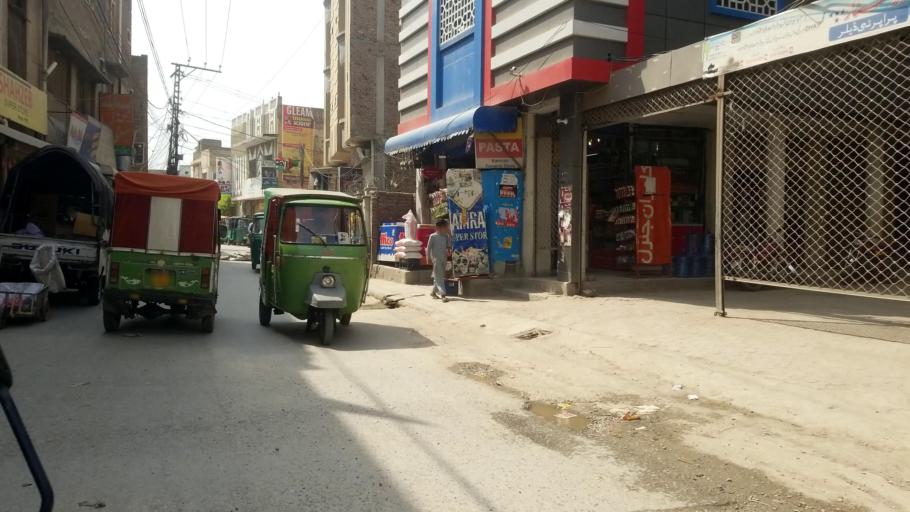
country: PK
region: Khyber Pakhtunkhwa
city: Peshawar
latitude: 33.9861
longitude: 71.5345
